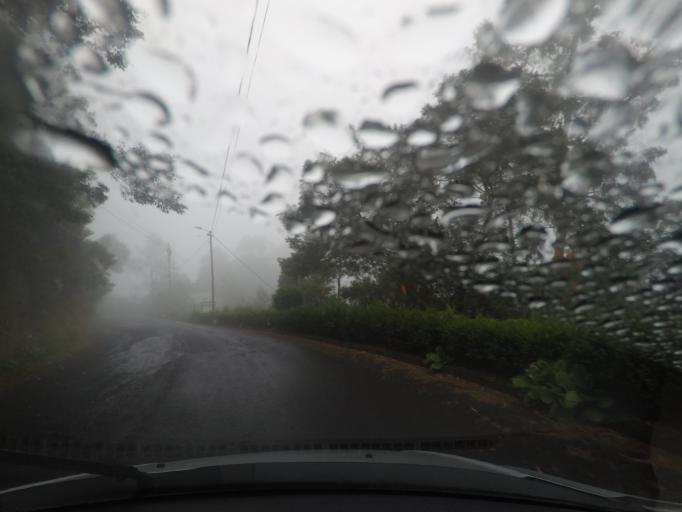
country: PT
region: Madeira
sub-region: Santana
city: Santana
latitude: 32.7566
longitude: -16.8679
